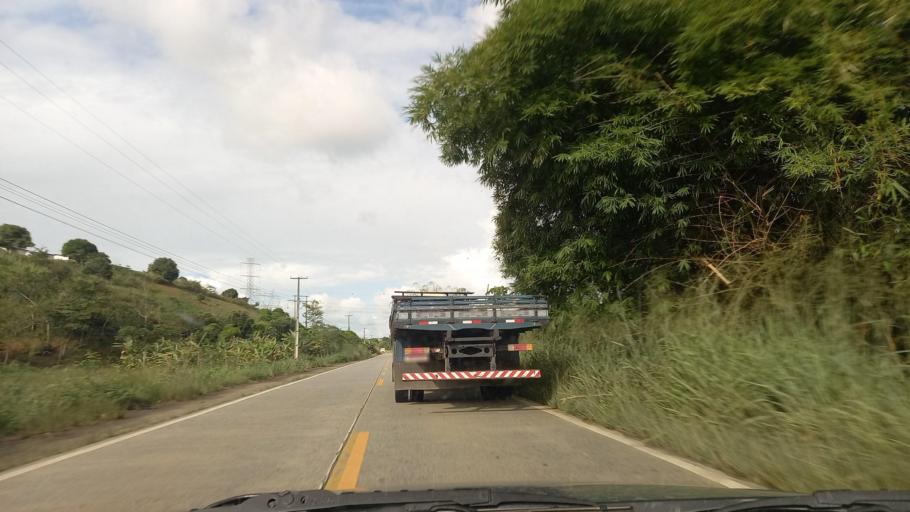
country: BR
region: Pernambuco
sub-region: Palmares
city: Palmares
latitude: -8.6913
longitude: -35.6192
